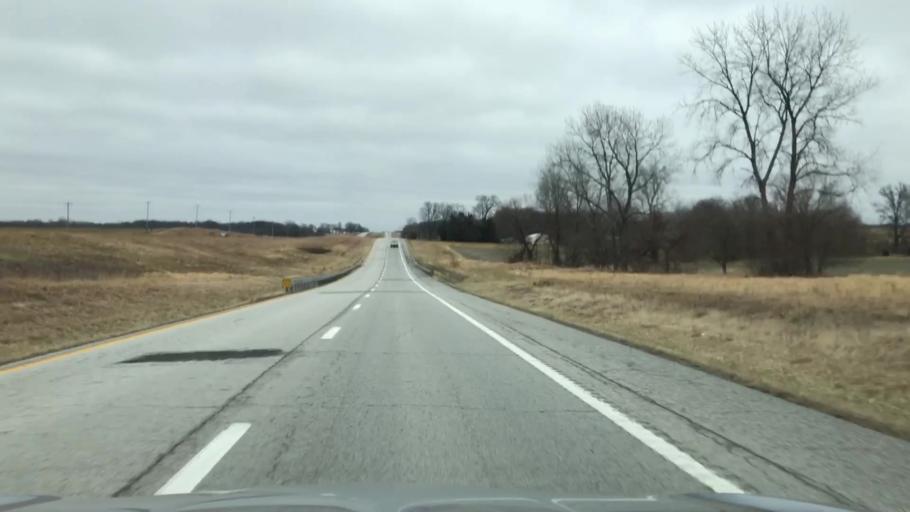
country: US
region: Missouri
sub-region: Linn County
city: Linneus
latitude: 39.7776
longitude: -93.2767
